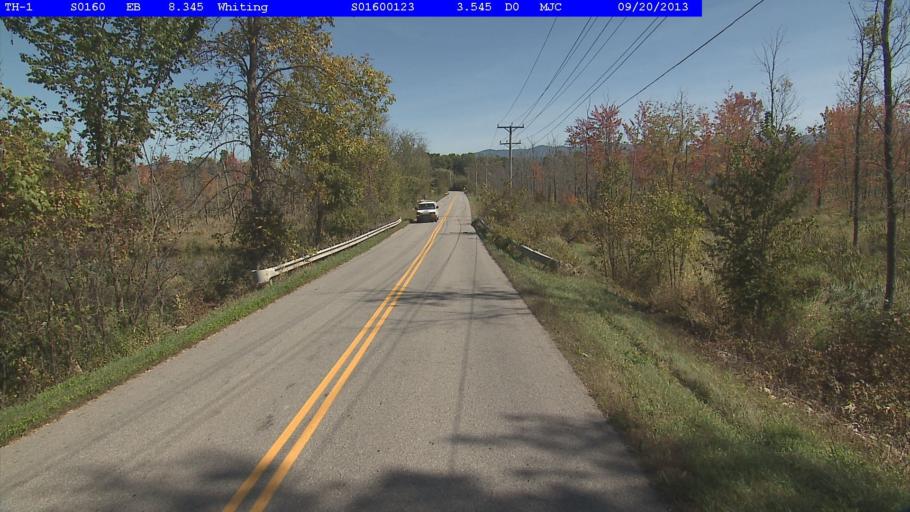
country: US
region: Vermont
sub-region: Rutland County
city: Brandon
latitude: 43.8516
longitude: -73.1599
